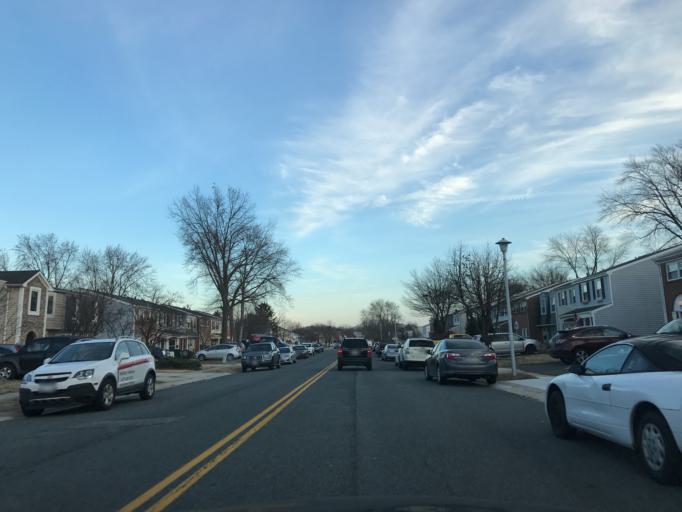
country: US
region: Maryland
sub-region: Harford County
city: Joppatowne
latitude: 39.4075
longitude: -76.3586
